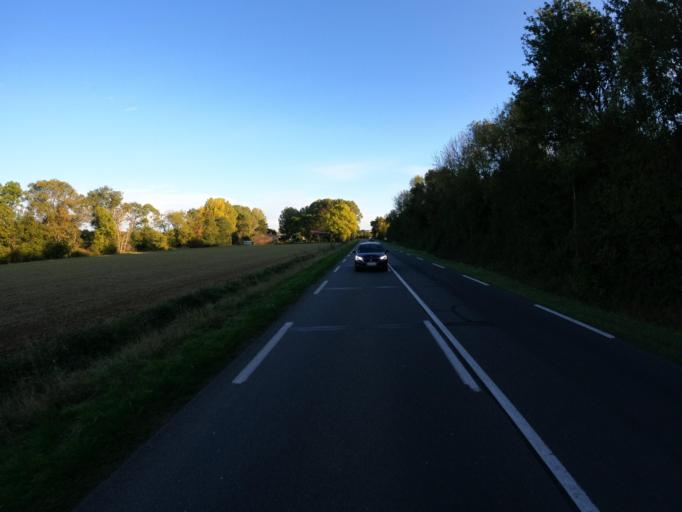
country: FR
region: Pays de la Loire
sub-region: Departement de la Vendee
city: Sainte-Hermine
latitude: 46.5803
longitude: -1.1098
